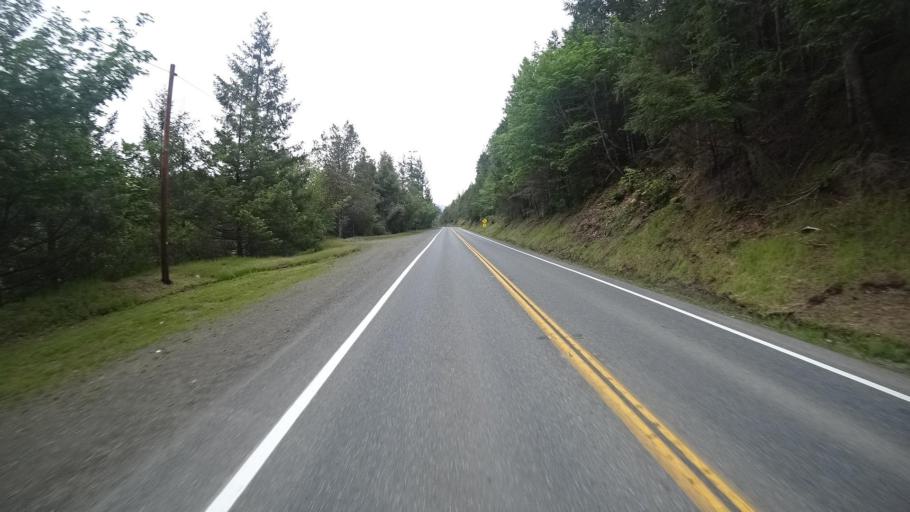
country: US
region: California
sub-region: Humboldt County
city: Willow Creek
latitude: 40.9987
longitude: -123.6396
